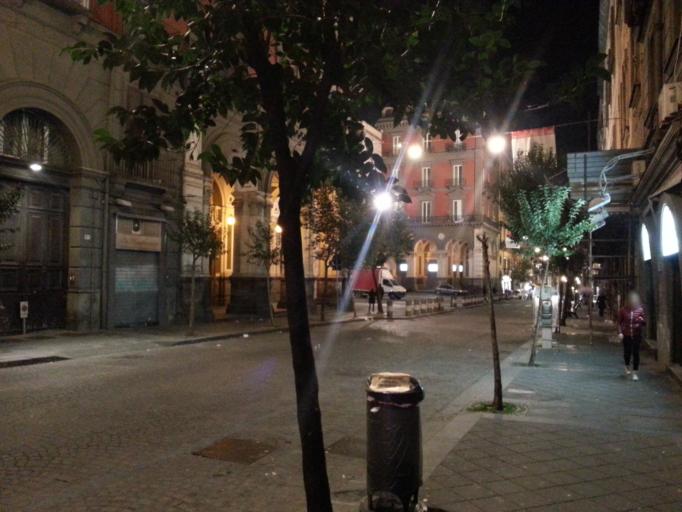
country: IT
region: Campania
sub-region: Provincia di Napoli
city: Napoli
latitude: 40.8529
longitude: 14.2588
